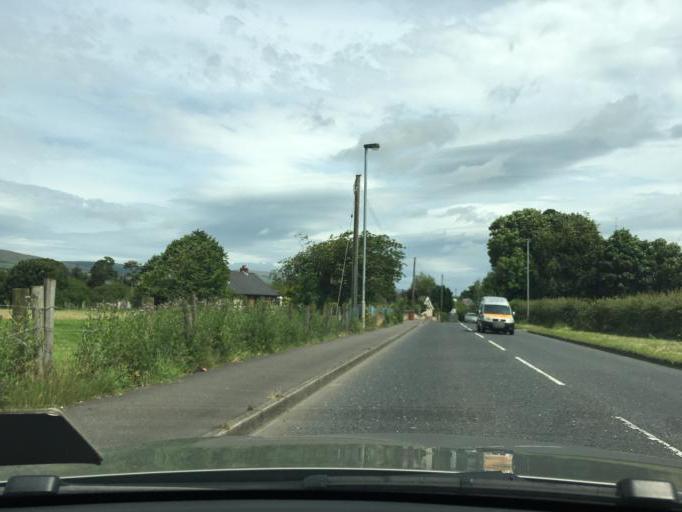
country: IE
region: Ulster
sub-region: County Donegal
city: Muff
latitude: 55.0623
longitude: -7.2714
